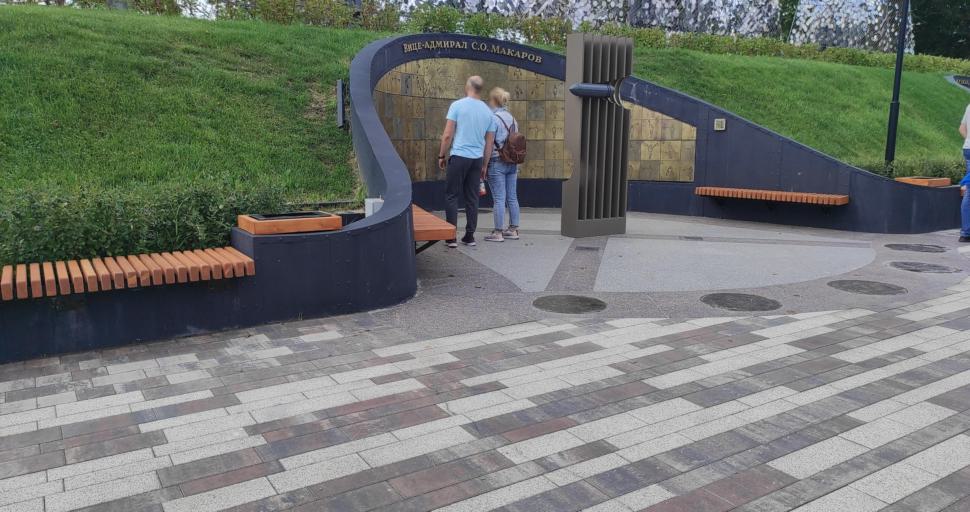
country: RU
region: St.-Petersburg
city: Kronshtadt
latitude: 59.9950
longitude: 29.7435
